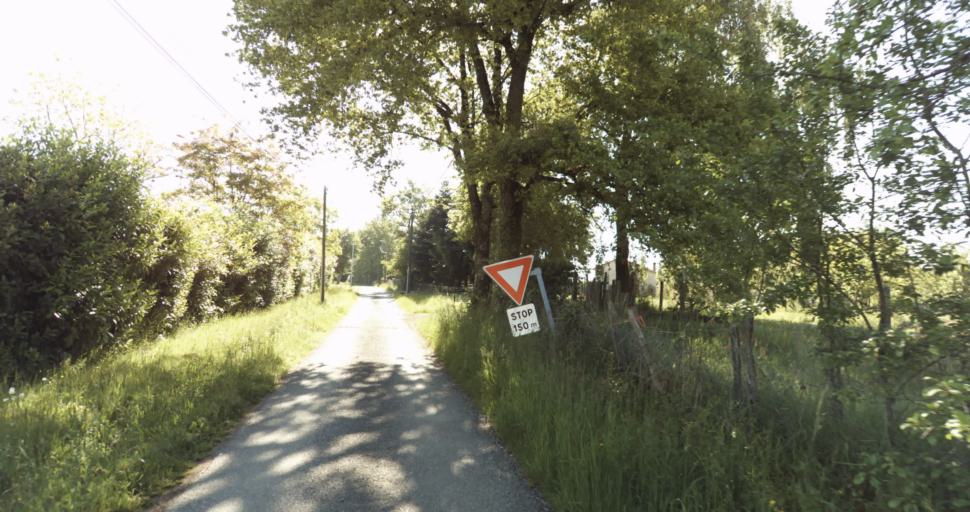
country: FR
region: Limousin
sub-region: Departement de la Haute-Vienne
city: Solignac
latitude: 45.7195
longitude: 1.2491
